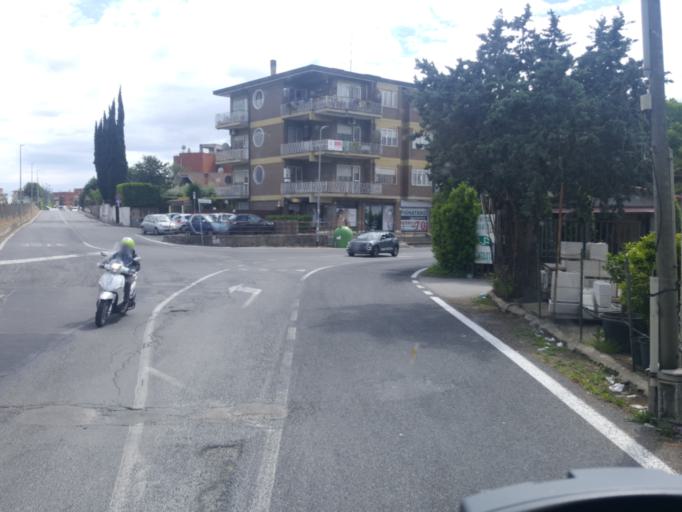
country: IT
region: Latium
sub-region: Citta metropolitana di Roma Capitale
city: La Massimina-Casal Lumbroso
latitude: 41.8842
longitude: 12.3614
